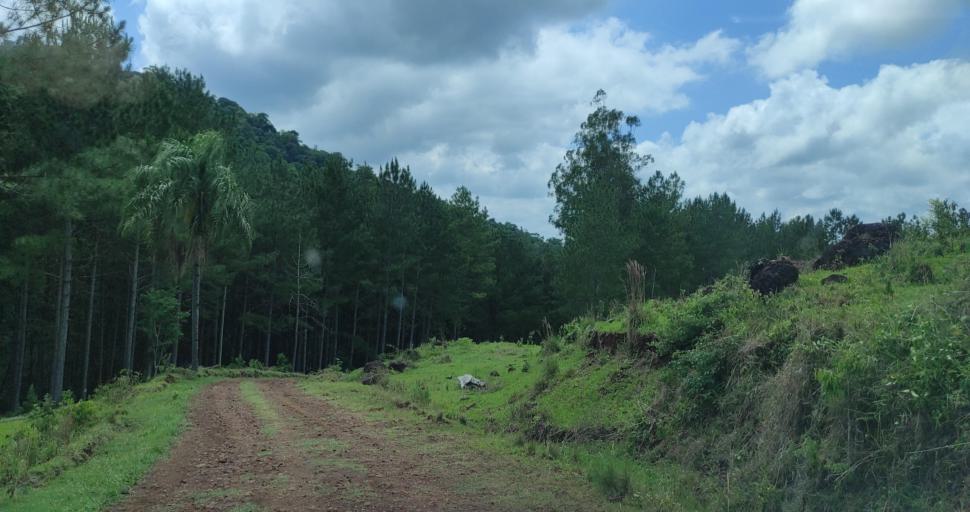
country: AR
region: Misiones
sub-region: Departamento de Veinticinco de Mayo
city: Veinticinco de Mayo
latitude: -27.4178
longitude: -54.7150
